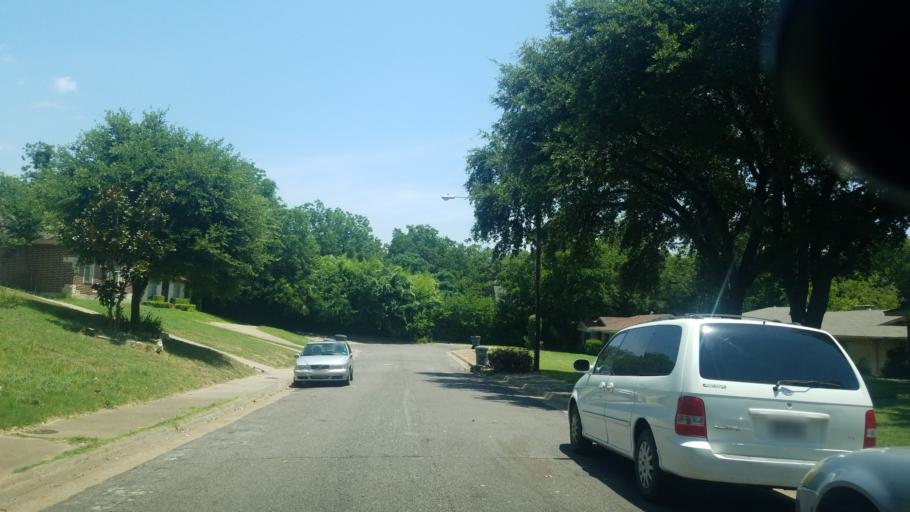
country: US
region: Texas
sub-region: Dallas County
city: Dallas
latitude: 32.7320
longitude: -96.7916
